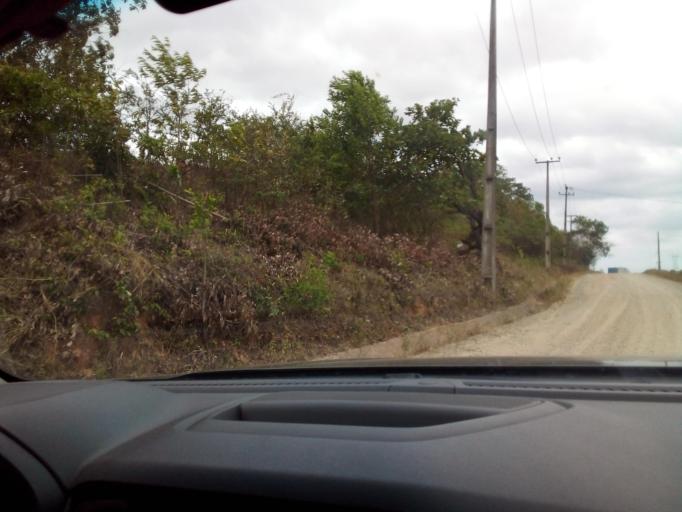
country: BR
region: Maranhao
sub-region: Sao Luis
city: Sao Luis
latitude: -2.6735
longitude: -44.2957
